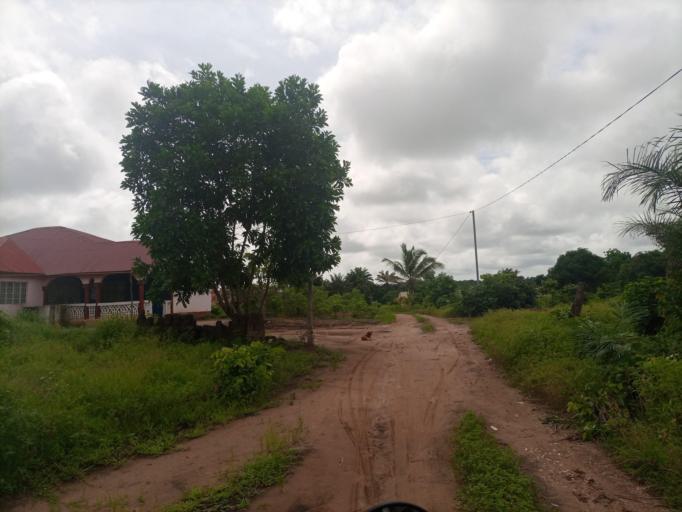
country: SL
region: Northern Province
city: Masoyila
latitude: 8.5929
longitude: -13.1760
